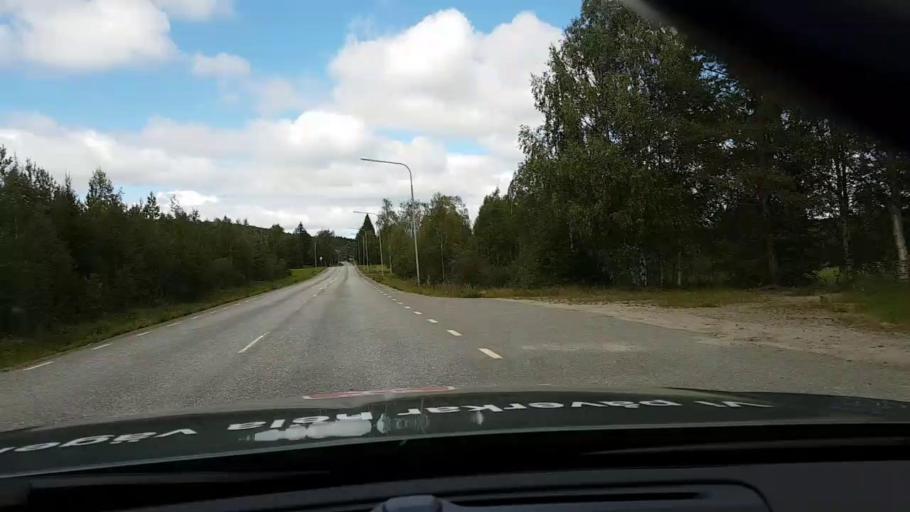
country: SE
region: Vaesternorrland
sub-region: OErnskoeldsviks Kommun
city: Bredbyn
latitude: 63.4830
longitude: 18.0890
